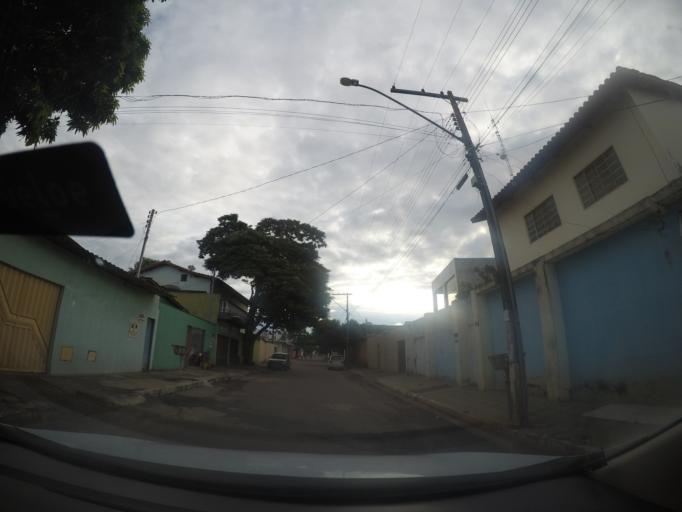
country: BR
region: Goias
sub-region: Goiania
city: Goiania
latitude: -16.6414
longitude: -49.3204
